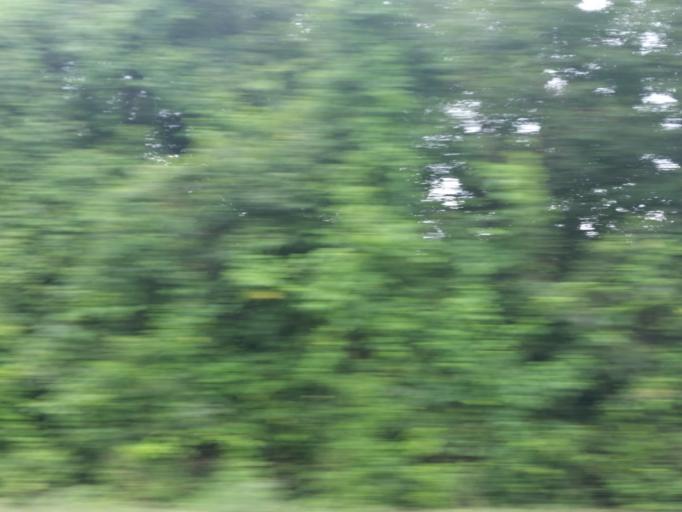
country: US
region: Kentucky
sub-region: Ballard County
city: Wickliffe
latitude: 36.9874
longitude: -89.1097
